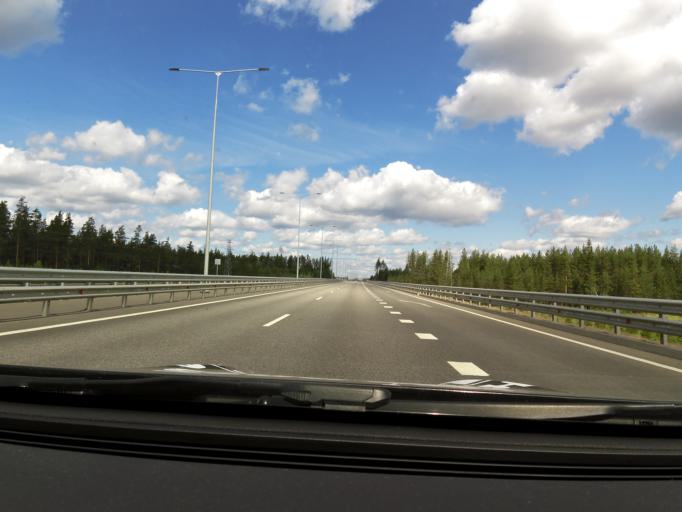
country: RU
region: Tverskaya
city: Krasnomayskiy
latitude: 57.5333
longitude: 34.2743
